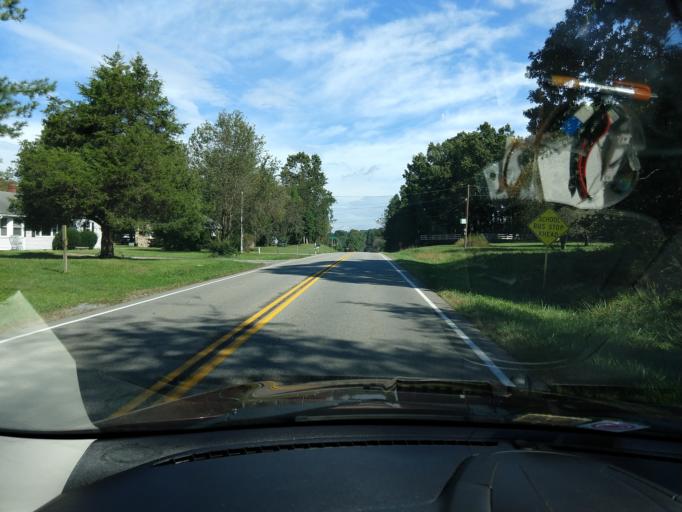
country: US
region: Virginia
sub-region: Augusta County
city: Crimora
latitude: 38.2087
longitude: -78.8328
